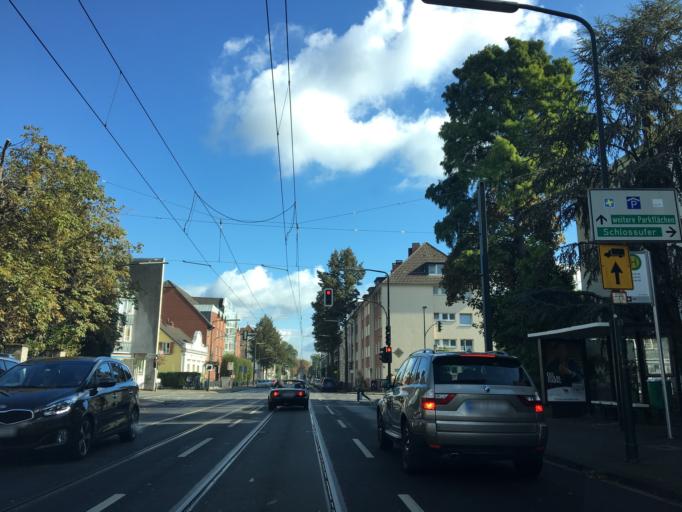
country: DE
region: North Rhine-Westphalia
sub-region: Regierungsbezirk Dusseldorf
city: Dormagen
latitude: 51.1622
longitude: 6.8595
